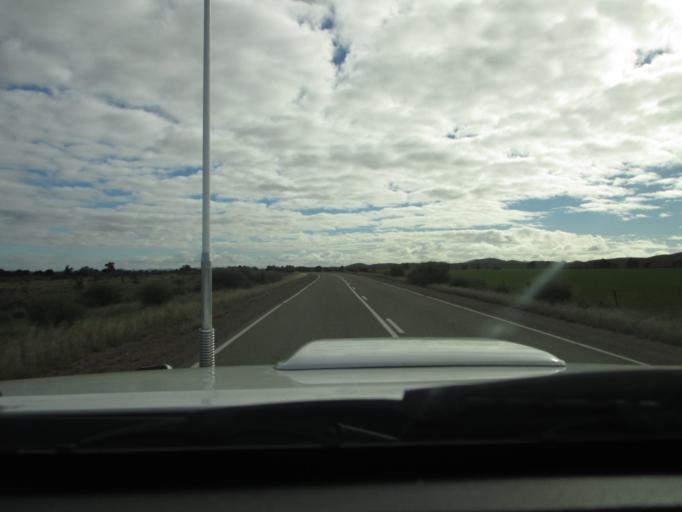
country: AU
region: South Australia
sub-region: Flinders Ranges
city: Quorn
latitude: -32.4394
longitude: 138.5356
